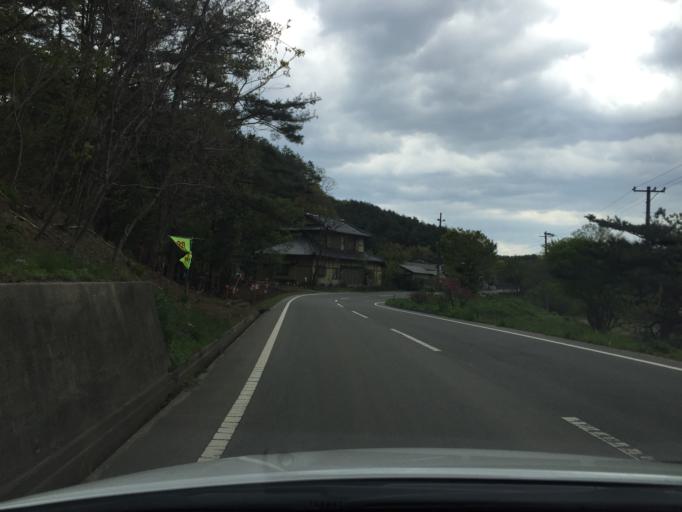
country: JP
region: Fukushima
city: Yanagawamachi-saiwaicho
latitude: 37.7111
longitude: 140.7379
